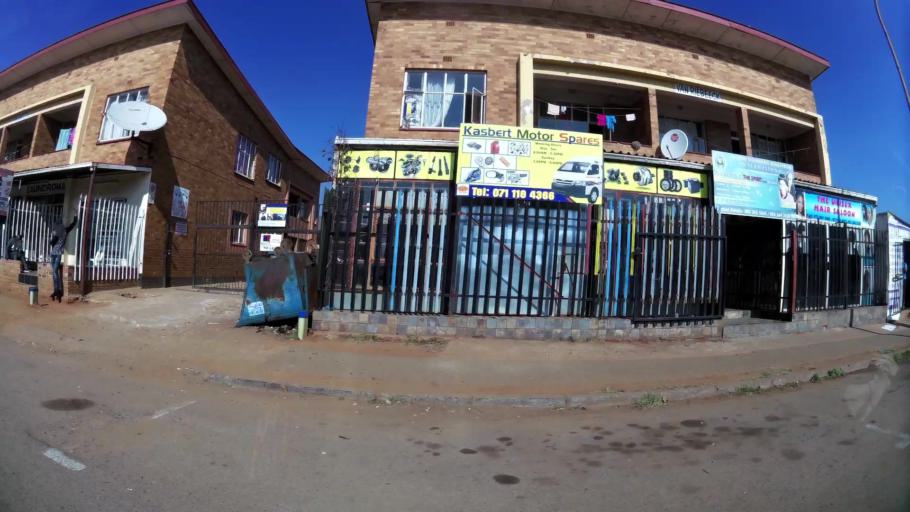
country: ZA
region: Gauteng
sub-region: City of Johannesburg Metropolitan Municipality
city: Modderfontein
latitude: -26.1073
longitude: 28.2358
